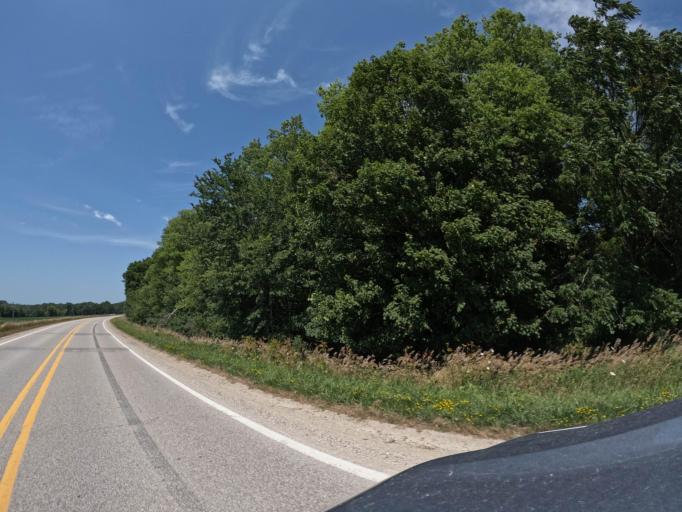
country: US
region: Iowa
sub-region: Henry County
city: Mount Pleasant
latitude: 40.9367
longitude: -91.6055
